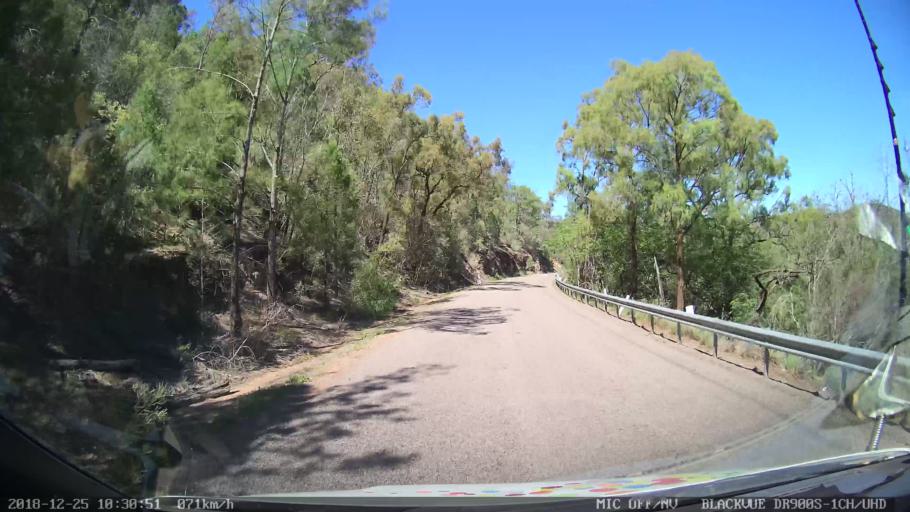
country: AU
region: New South Wales
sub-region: Muswellbrook
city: Denman
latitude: -32.3851
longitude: 150.4345
